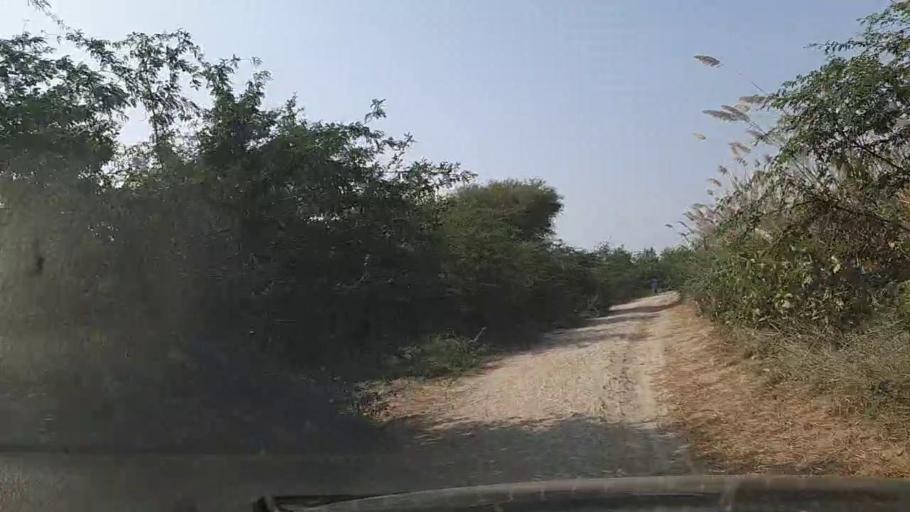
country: PK
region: Sindh
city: Gharo
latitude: 24.7039
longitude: 67.6459
